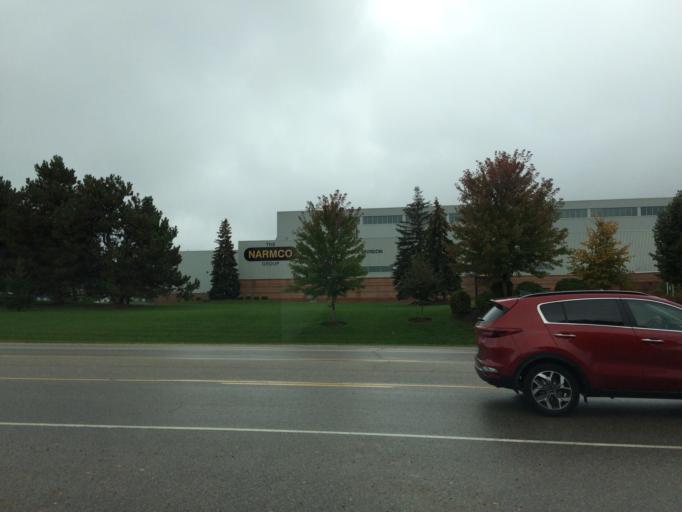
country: CA
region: Ontario
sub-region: Wellington County
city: Guelph
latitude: 43.5339
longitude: -80.3077
